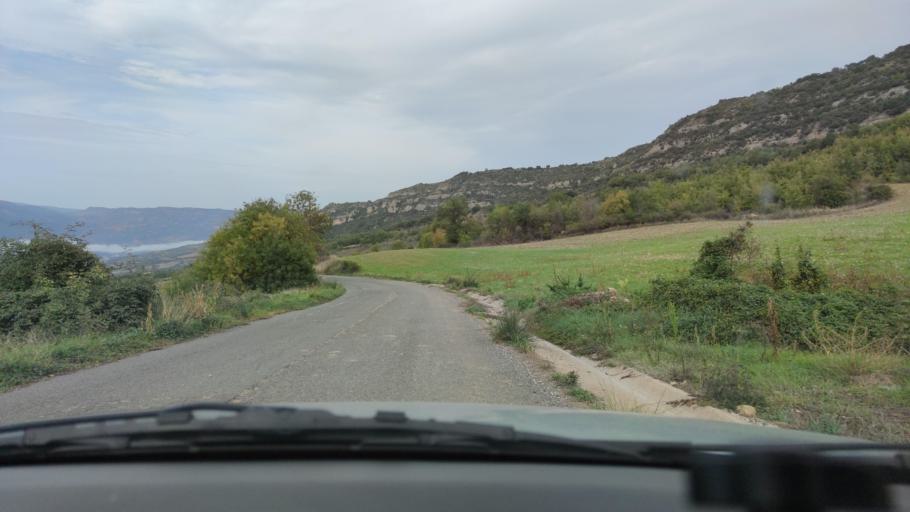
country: ES
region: Catalonia
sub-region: Provincia de Lleida
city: Llimiana
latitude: 42.0497
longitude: 0.9917
